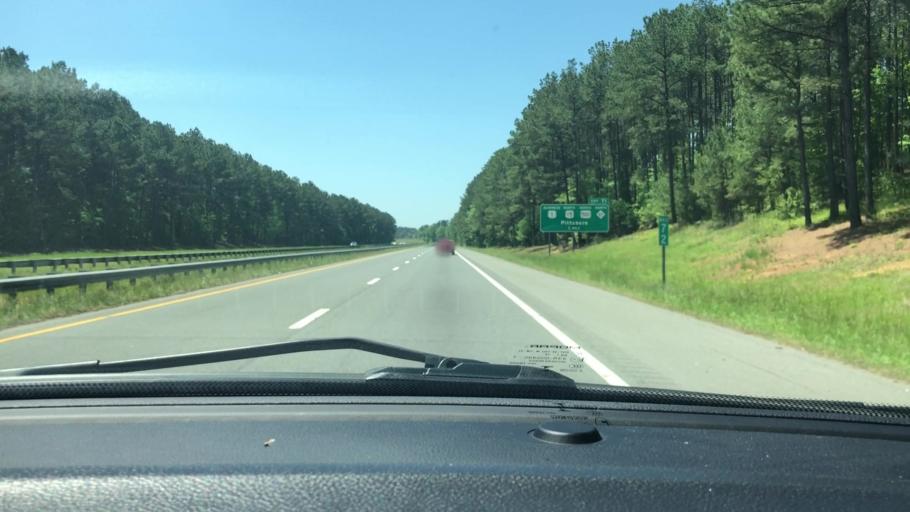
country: US
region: North Carolina
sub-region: Chatham County
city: Farmville
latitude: 35.5406
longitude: -79.1722
